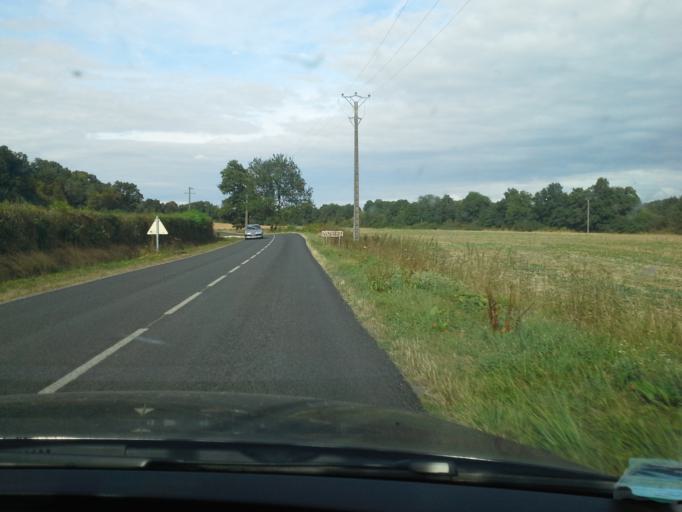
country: FR
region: Centre
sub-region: Departement d'Indre-et-Loire
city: Reugny
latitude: 47.4869
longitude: 0.8875
